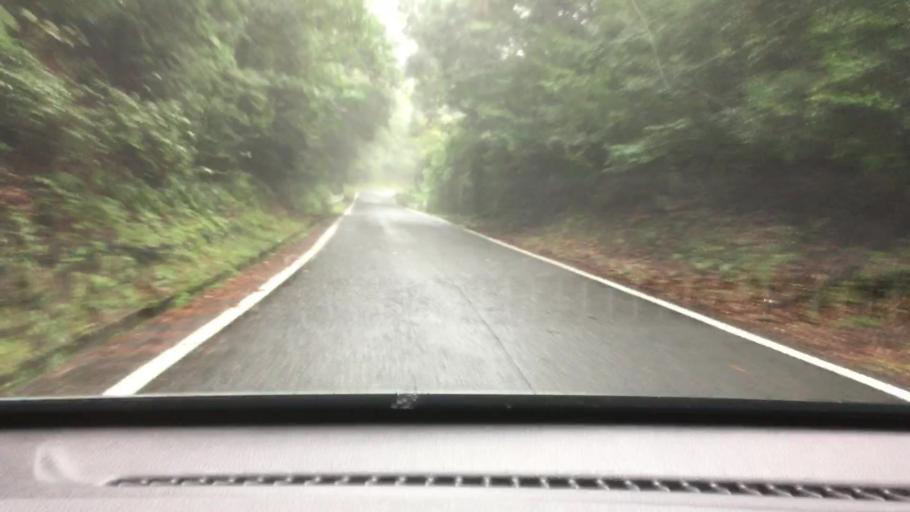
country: JP
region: Nagasaki
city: Togitsu
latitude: 32.9161
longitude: 129.7339
